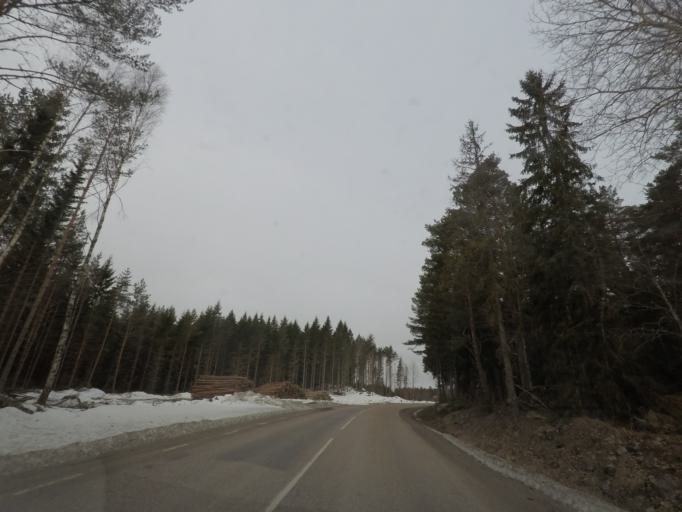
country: SE
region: Vaestmanland
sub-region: Vasteras
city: Skultuna
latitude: 59.7408
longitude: 16.3852
